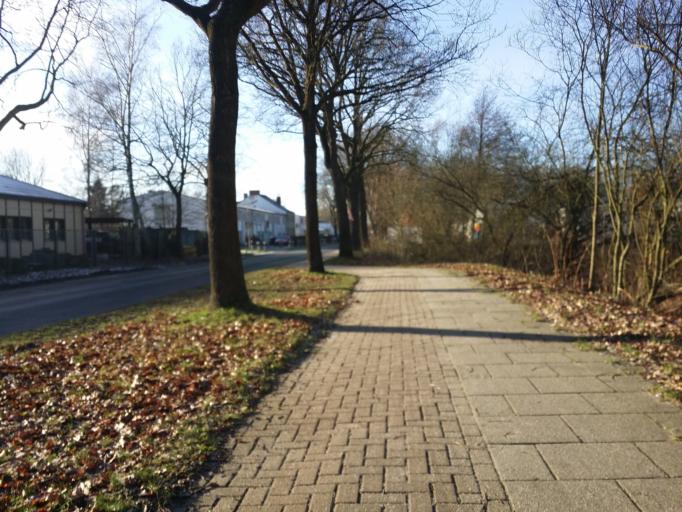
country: DE
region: Lower Saxony
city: Stuhr
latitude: 53.0632
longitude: 8.7451
